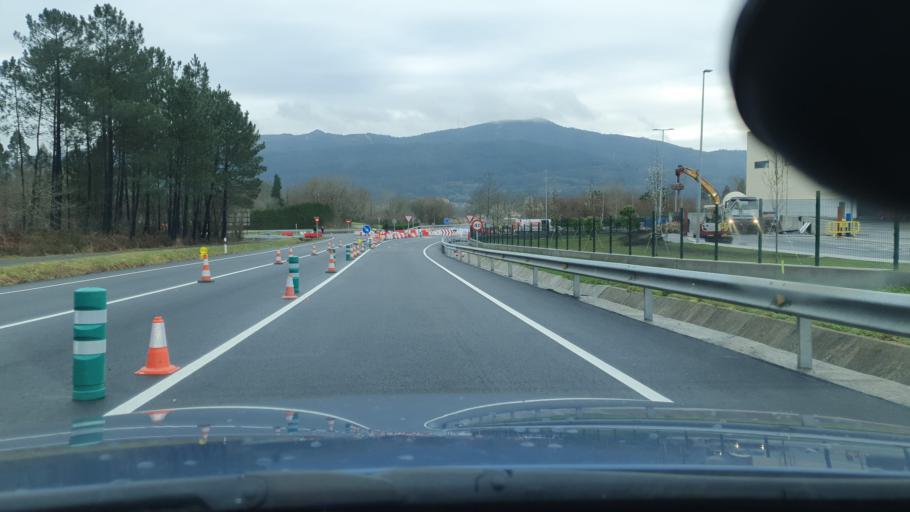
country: ES
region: Galicia
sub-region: Provincia da Coruna
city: Padron
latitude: 42.7573
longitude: -8.6719
